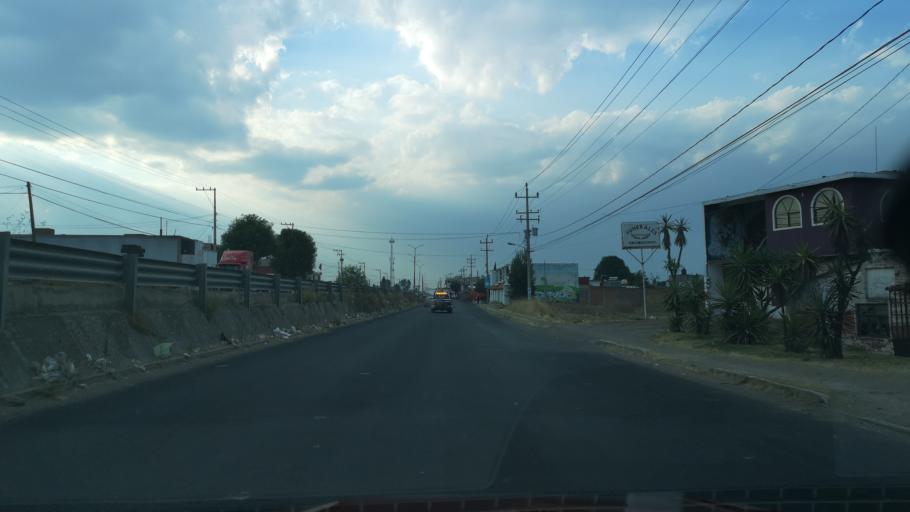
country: MX
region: Puebla
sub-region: Juan C. Bonilla
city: Santa Maria Zacatepec
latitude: 19.1166
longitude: -98.3596
